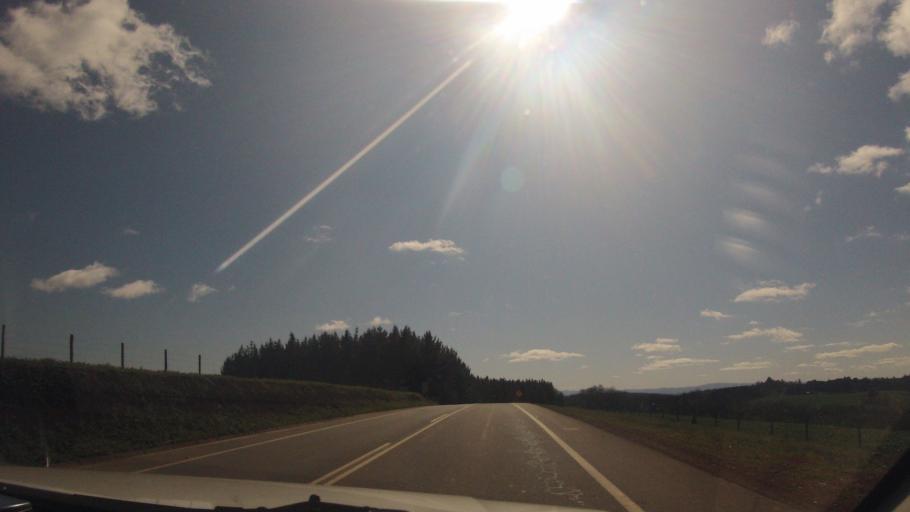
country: CL
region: Araucania
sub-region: Provincia de Malleco
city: Traiguen
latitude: -38.2010
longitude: -72.8003
